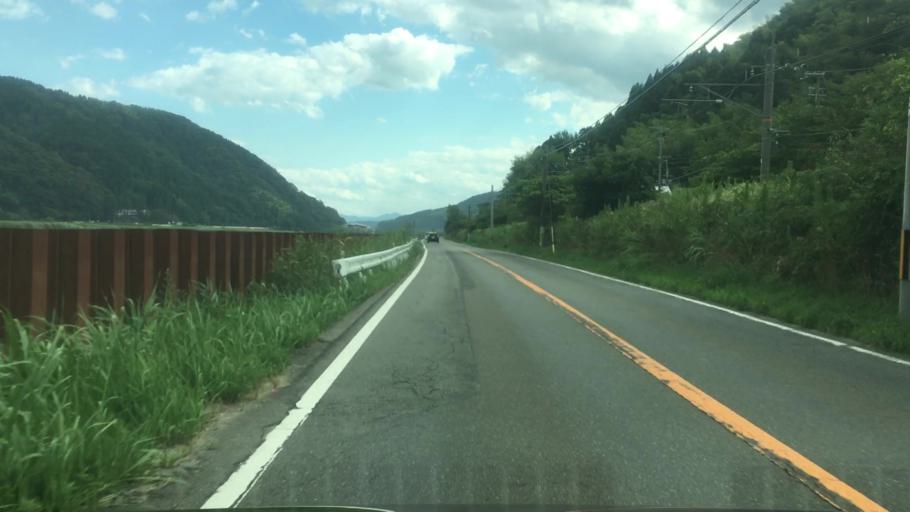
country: JP
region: Hyogo
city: Toyooka
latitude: 35.6016
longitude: 134.8017
